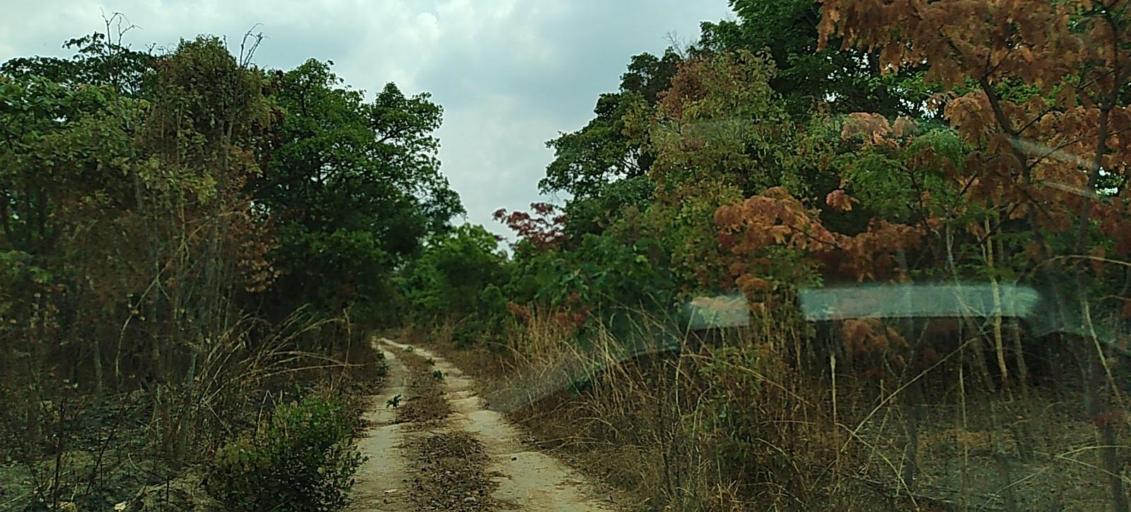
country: ZM
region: Copperbelt
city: Chililabombwe
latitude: -12.3270
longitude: 27.7710
